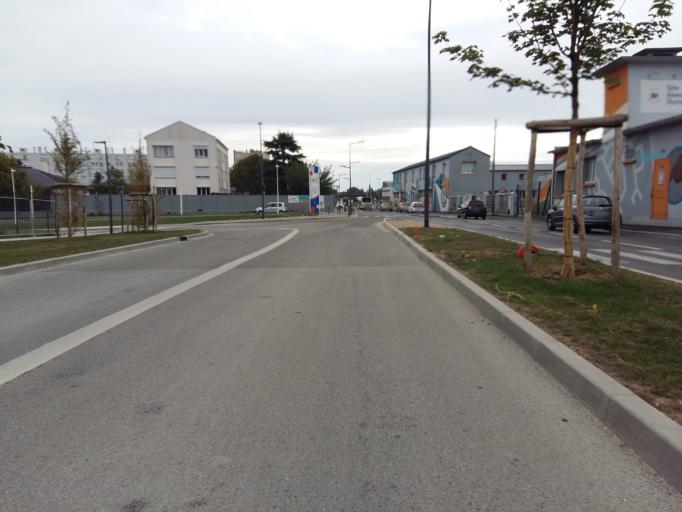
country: FR
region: Picardie
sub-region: Departement de la Somme
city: Amiens
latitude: 49.8714
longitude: 2.3004
